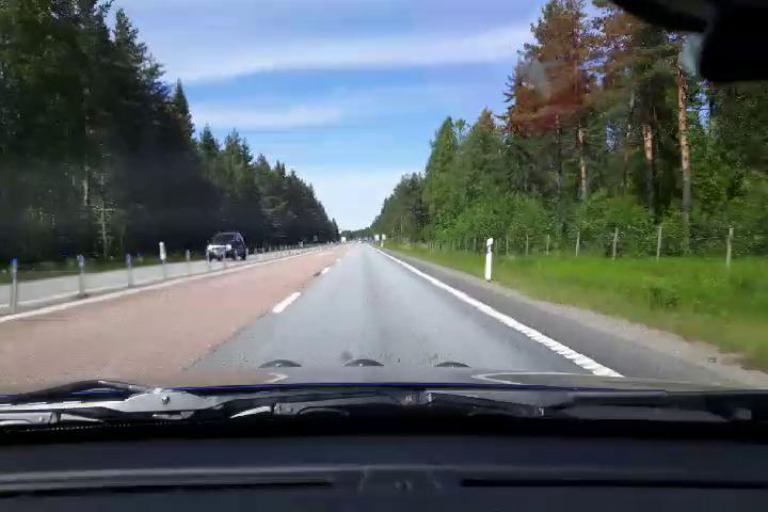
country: SE
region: Gaevleborg
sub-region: Gavle Kommun
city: Norrsundet
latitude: 61.0557
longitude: 16.9598
